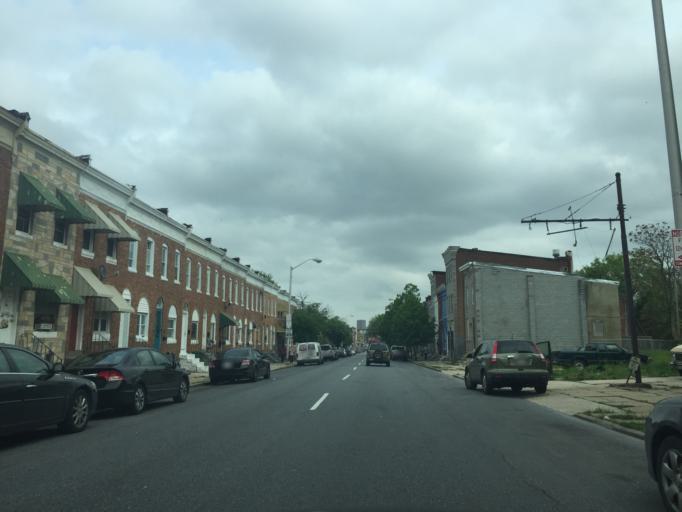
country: US
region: Maryland
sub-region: City of Baltimore
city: Baltimore
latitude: 39.3130
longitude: -76.6408
